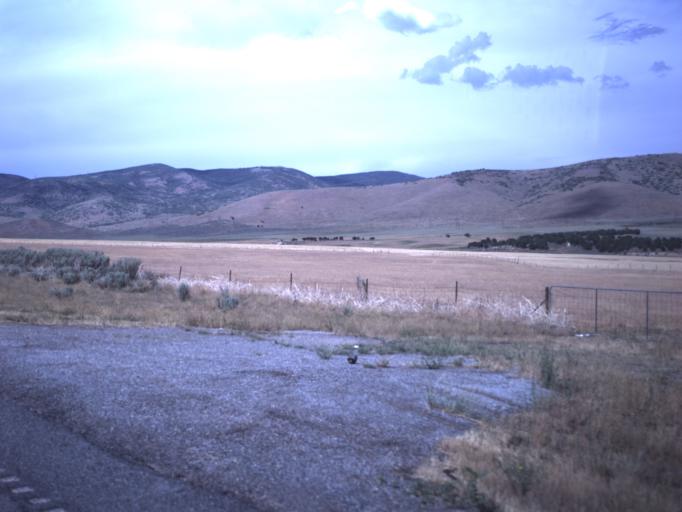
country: US
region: Utah
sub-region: Sanpete County
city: Fountain Green
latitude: 39.6626
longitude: -111.6567
